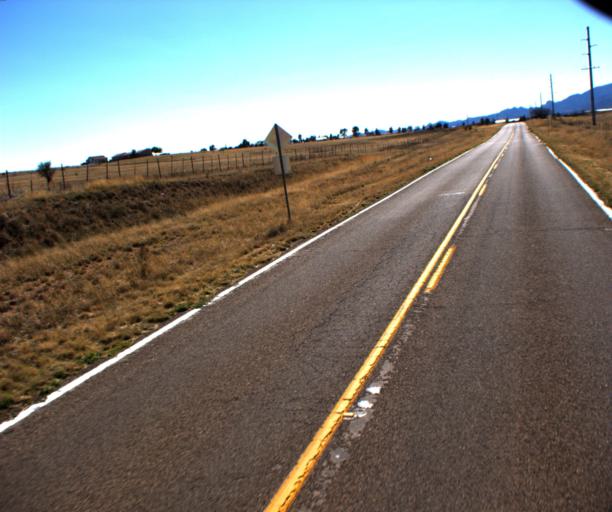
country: US
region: Arizona
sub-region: Cochise County
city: Huachuca City
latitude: 31.6755
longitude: -110.6418
